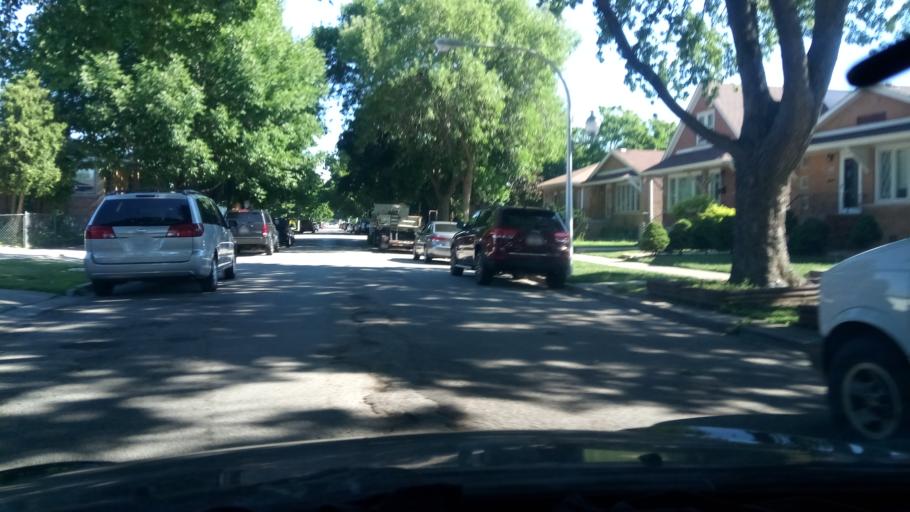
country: US
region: Illinois
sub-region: Cook County
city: Hometown
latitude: 41.7722
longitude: -87.7346
